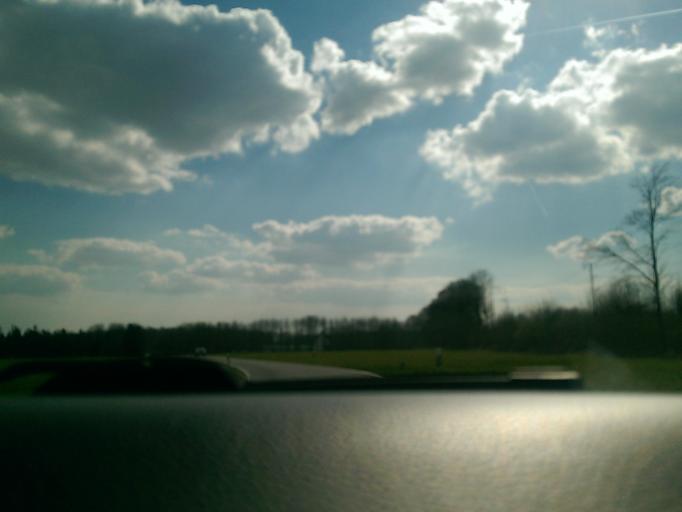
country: DE
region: North Rhine-Westphalia
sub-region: Regierungsbezirk Munster
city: Muenster
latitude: 51.9474
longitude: 7.6779
